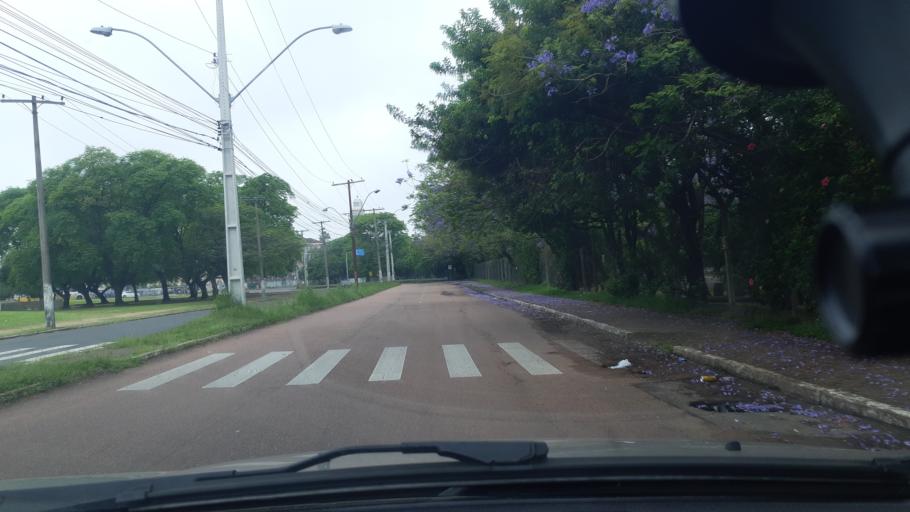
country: BR
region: Rio Grande do Sul
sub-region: Porto Alegre
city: Porto Alegre
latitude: -30.0392
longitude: -51.2302
